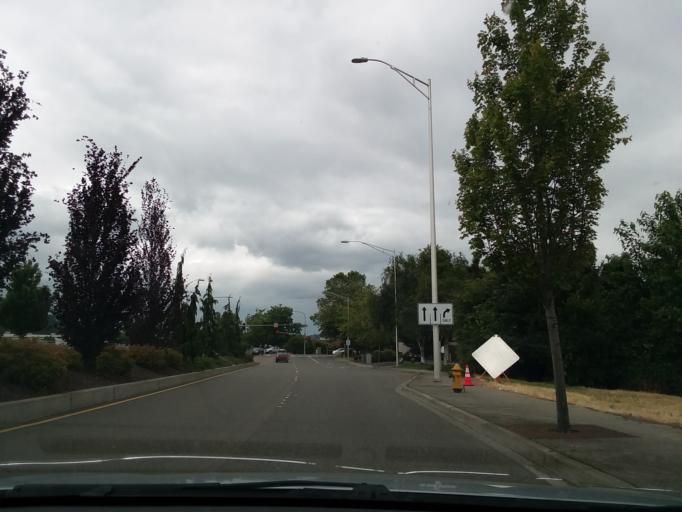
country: US
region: Washington
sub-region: King County
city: SeaTac
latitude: 47.4401
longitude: -122.2607
